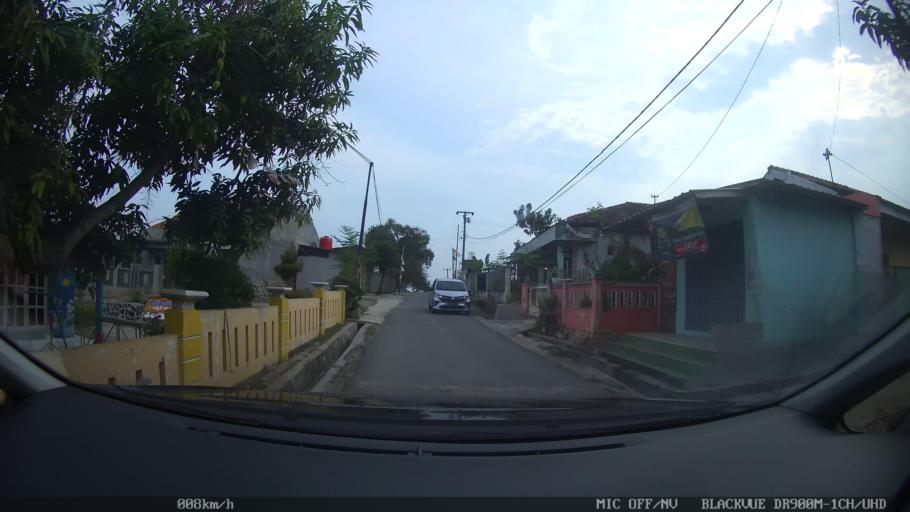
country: ID
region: Lampung
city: Panjang
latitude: -5.4378
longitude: 105.3006
